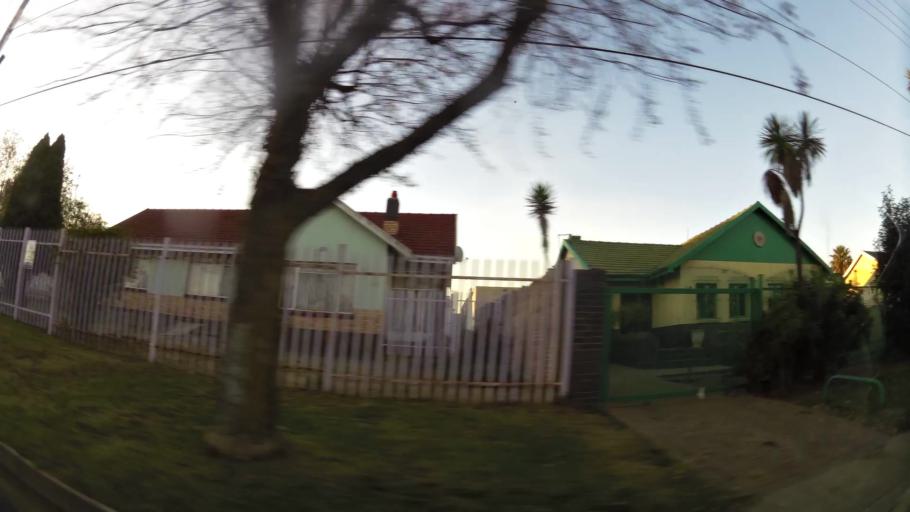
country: ZA
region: Gauteng
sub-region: City of Johannesburg Metropolitan Municipality
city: Roodepoort
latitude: -26.1532
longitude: 27.8873
